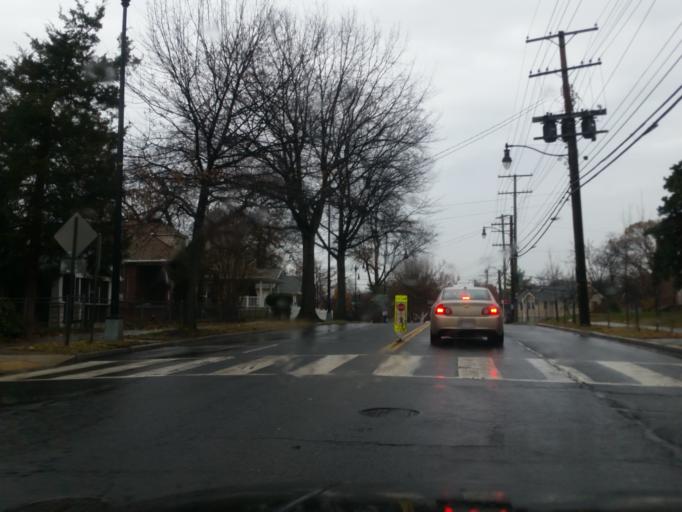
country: US
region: Maryland
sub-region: Prince George's County
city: Coral Hills
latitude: 38.8828
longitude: -76.9581
